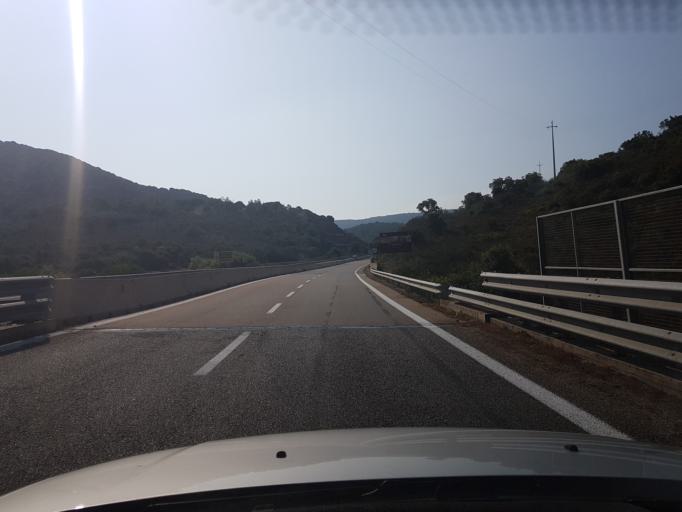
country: IT
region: Sardinia
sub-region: Provincia di Olbia-Tempio
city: Loiri Porto San Paolo
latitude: 40.8290
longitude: 9.5742
